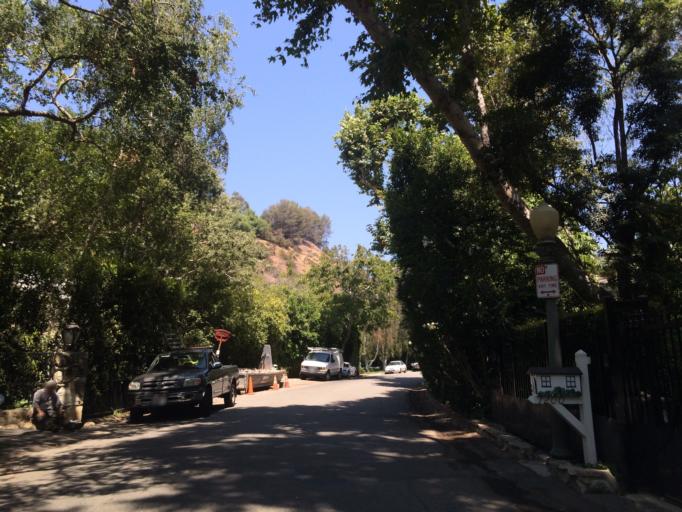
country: US
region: California
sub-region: Los Angeles County
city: Westwood, Los Angeles
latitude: 34.0957
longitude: -118.4496
